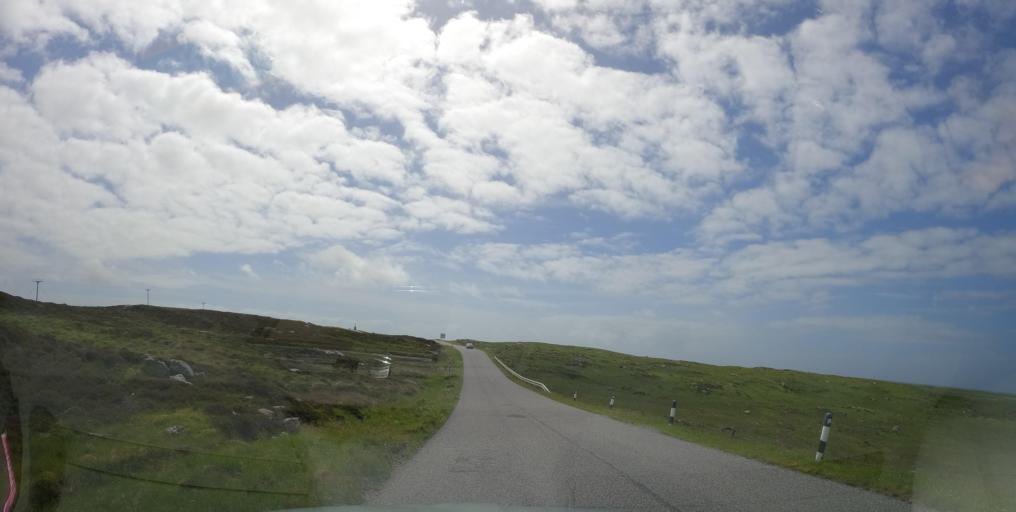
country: GB
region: Scotland
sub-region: Eilean Siar
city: Isle of South Uist
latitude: 57.2341
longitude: -7.3973
